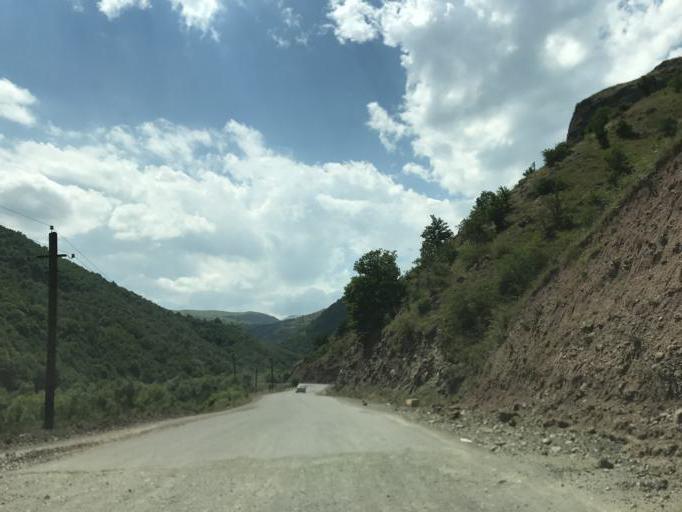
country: AZ
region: Kalbacar Rayonu
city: Kerbakhiar
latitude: 40.2313
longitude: 46.0986
